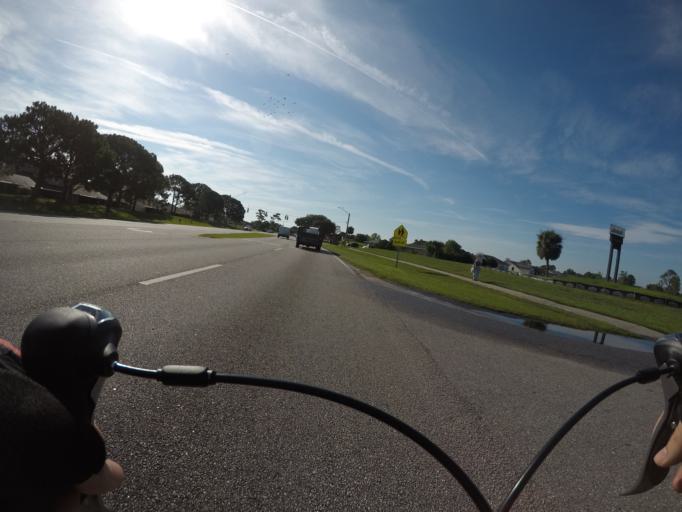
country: US
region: Florida
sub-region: Osceola County
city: Buenaventura Lakes
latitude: 28.3388
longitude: -81.3611
